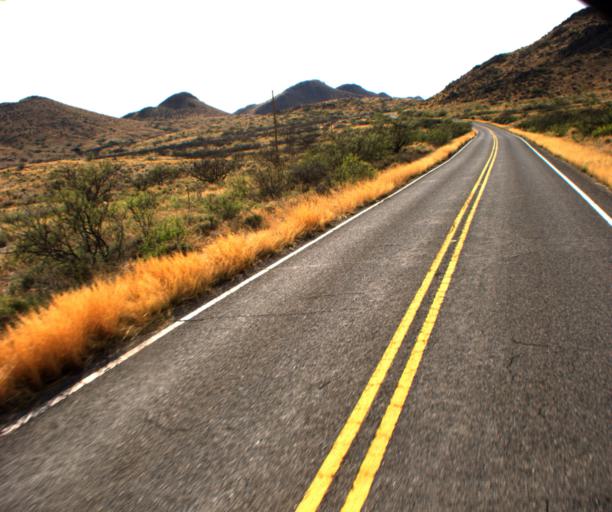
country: US
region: Arizona
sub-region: Cochise County
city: Willcox
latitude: 32.1667
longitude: -109.5816
